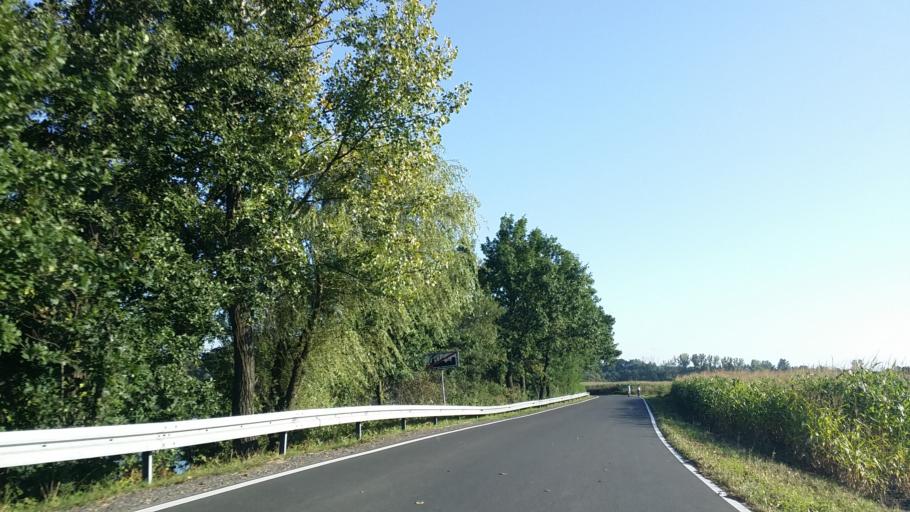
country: PL
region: Lesser Poland Voivodeship
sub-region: Powiat wadowicki
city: Spytkowice
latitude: 50.0151
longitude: 19.5127
